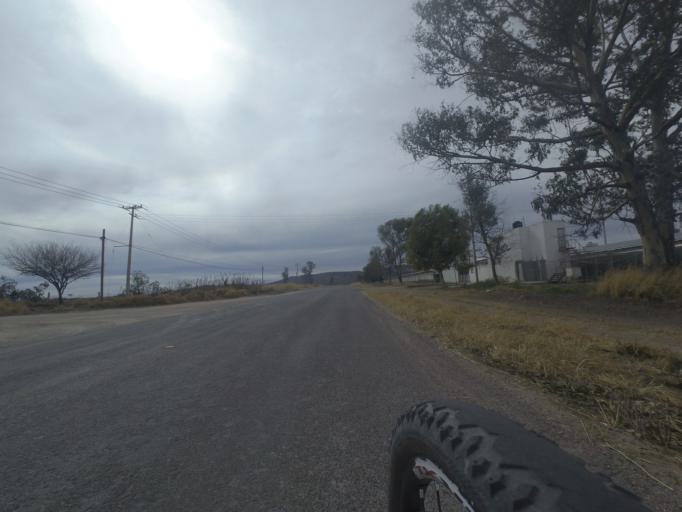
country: MX
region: Aguascalientes
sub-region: Aguascalientes
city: La Loma de los Negritos
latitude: 21.8372
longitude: -102.3585
